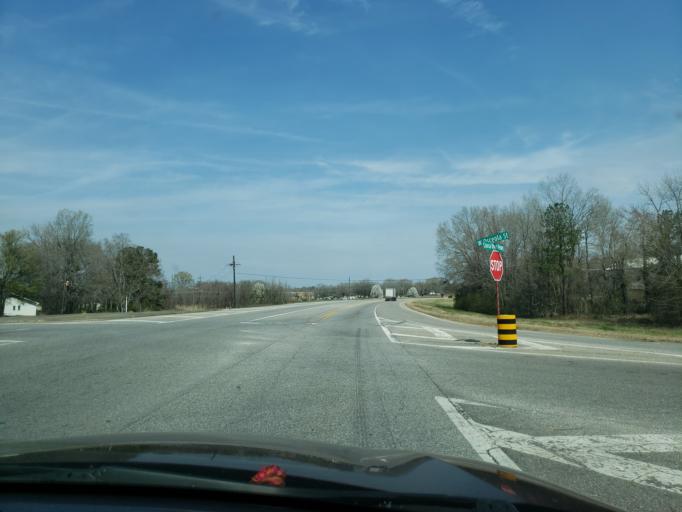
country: US
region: Alabama
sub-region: Elmore County
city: Wetumpka
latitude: 32.5472
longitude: -86.2242
